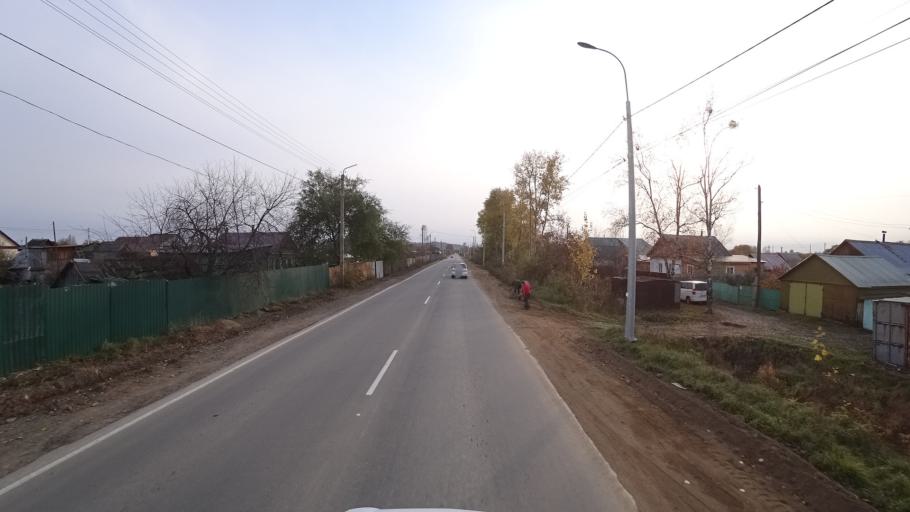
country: RU
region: Khabarovsk Krai
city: Amursk
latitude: 50.0876
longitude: 136.5004
